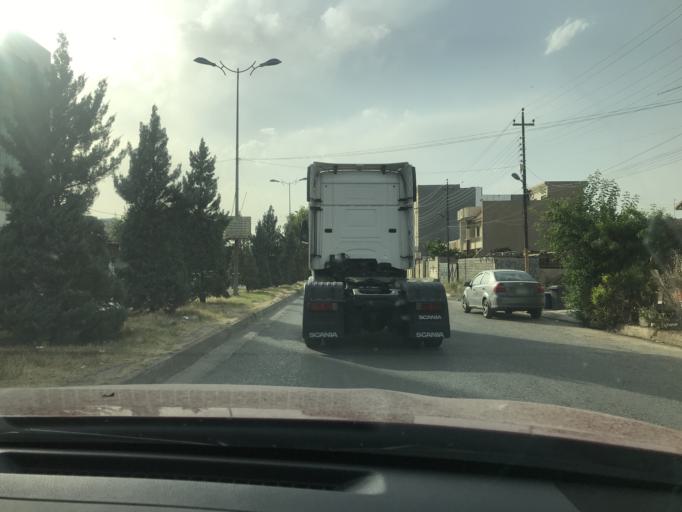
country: IQ
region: Arbil
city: Erbil
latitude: 36.1784
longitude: 43.9793
